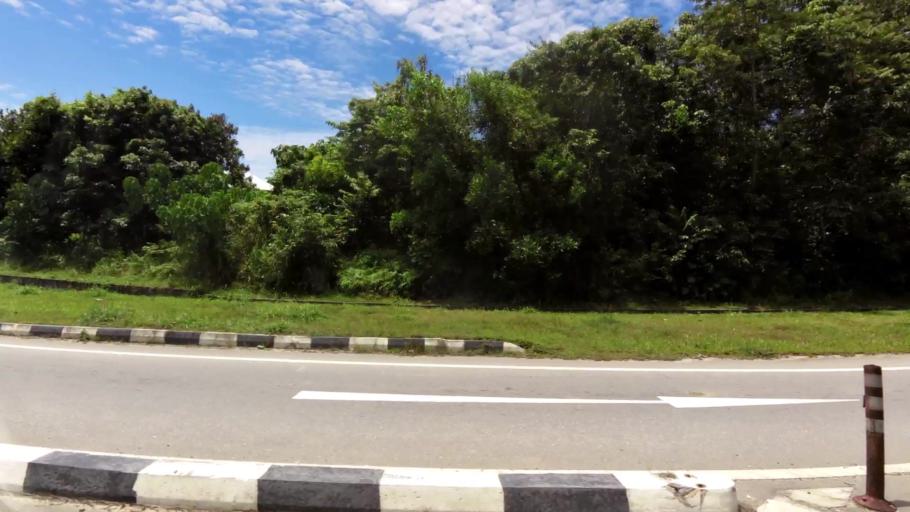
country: BN
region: Brunei and Muara
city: Bandar Seri Begawan
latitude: 4.9977
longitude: 115.0230
